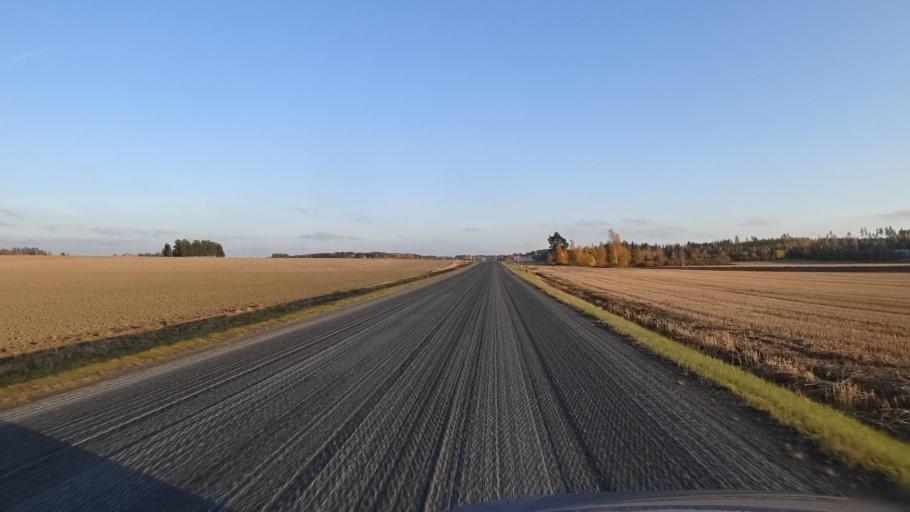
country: FI
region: Haeme
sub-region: Forssa
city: Ypaejae
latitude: 60.7897
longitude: 23.2894
